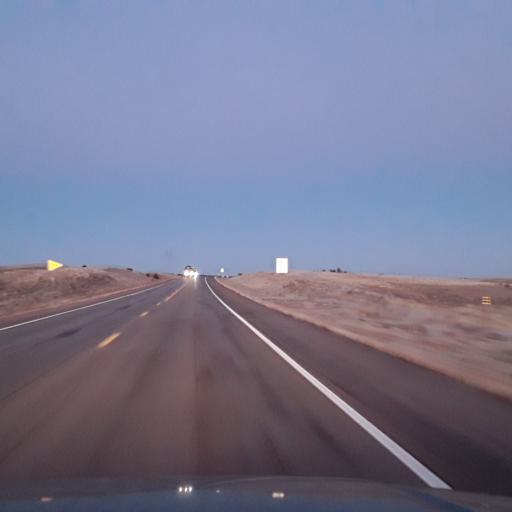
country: US
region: New Mexico
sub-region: Guadalupe County
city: Santa Rosa
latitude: 34.7444
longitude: -105.0195
